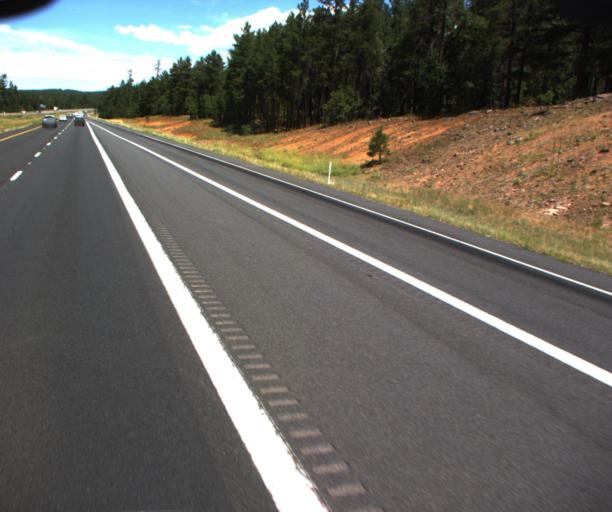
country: US
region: Arizona
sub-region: Coconino County
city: Sedona
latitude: 34.8783
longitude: -111.6369
